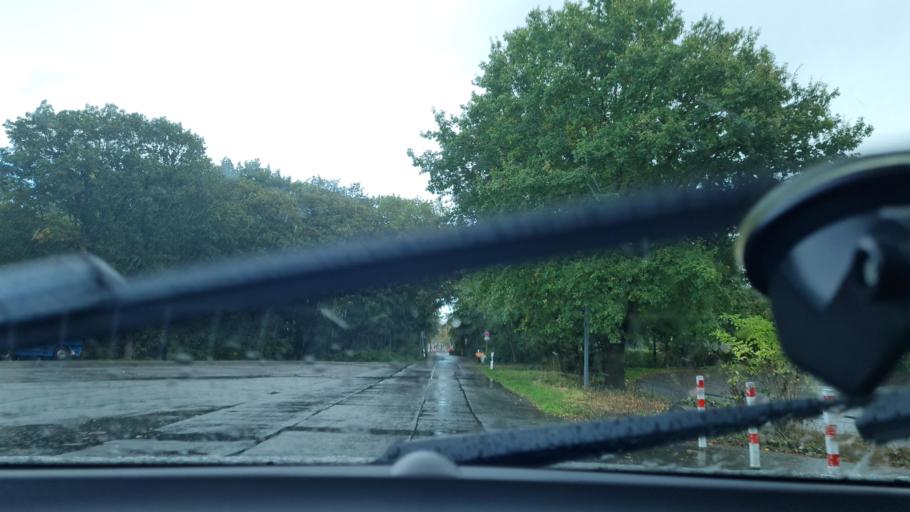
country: DE
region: North Rhine-Westphalia
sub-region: Regierungsbezirk Dusseldorf
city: Dinslaken
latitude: 51.5536
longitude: 6.7346
